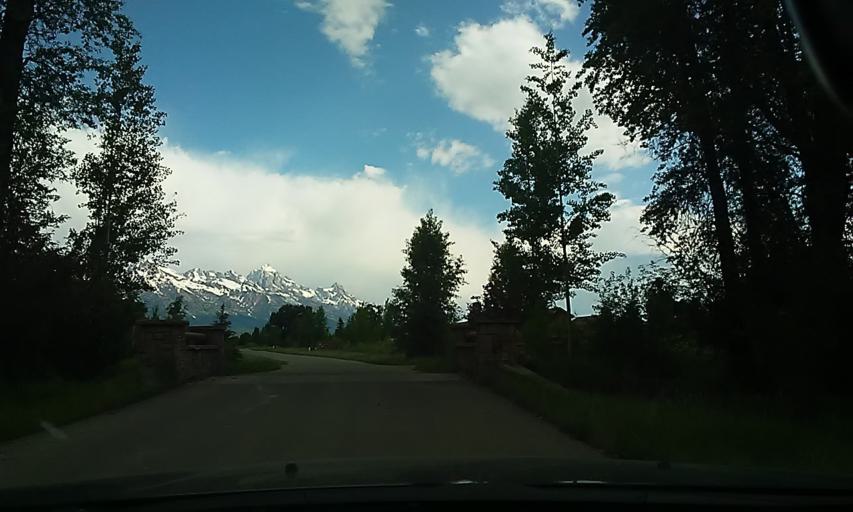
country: US
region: Wyoming
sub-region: Teton County
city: Jackson
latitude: 43.5599
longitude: -110.7646
